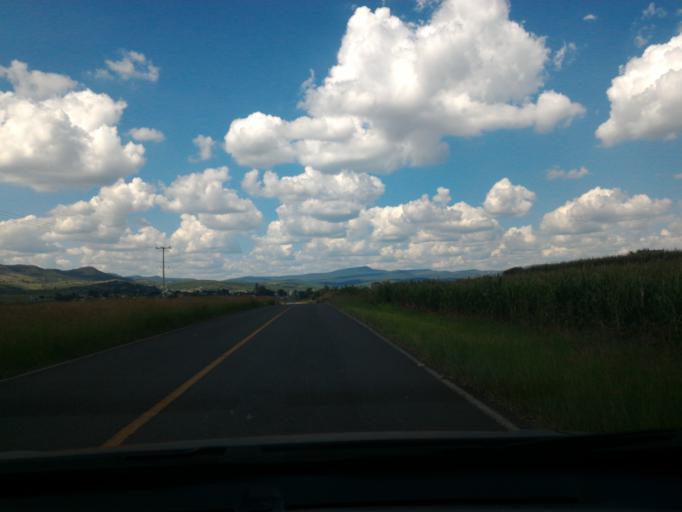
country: MX
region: Guanajuato
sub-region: Penjamo
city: Estacion la Piedad
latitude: 20.4427
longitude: -101.9860
